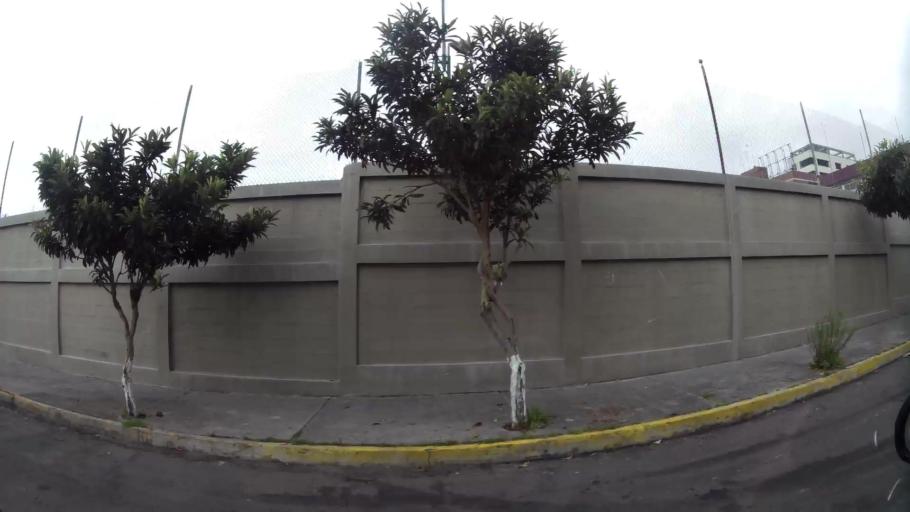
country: EC
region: Pichincha
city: Quito
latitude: -0.1920
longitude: -78.4898
